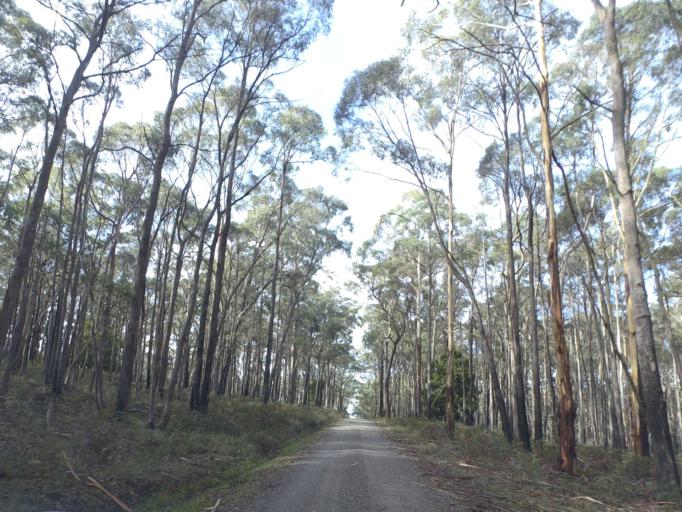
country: AU
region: Victoria
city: Brown Hill
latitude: -37.4784
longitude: 144.1663
